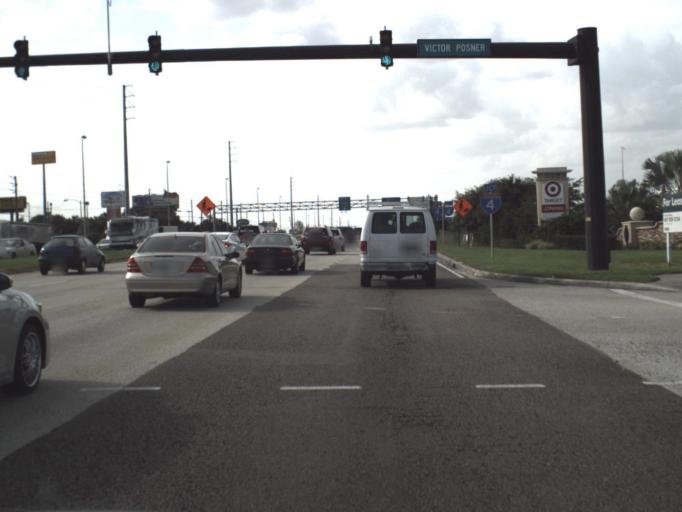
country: US
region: Florida
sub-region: Polk County
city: Davenport
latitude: 28.2250
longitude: -81.6452
